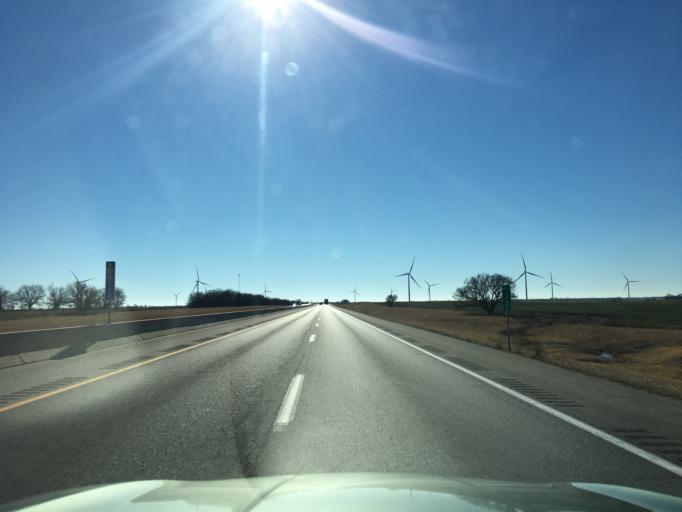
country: US
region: Kansas
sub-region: Sumner County
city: Wellington
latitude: 37.1584
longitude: -97.3395
